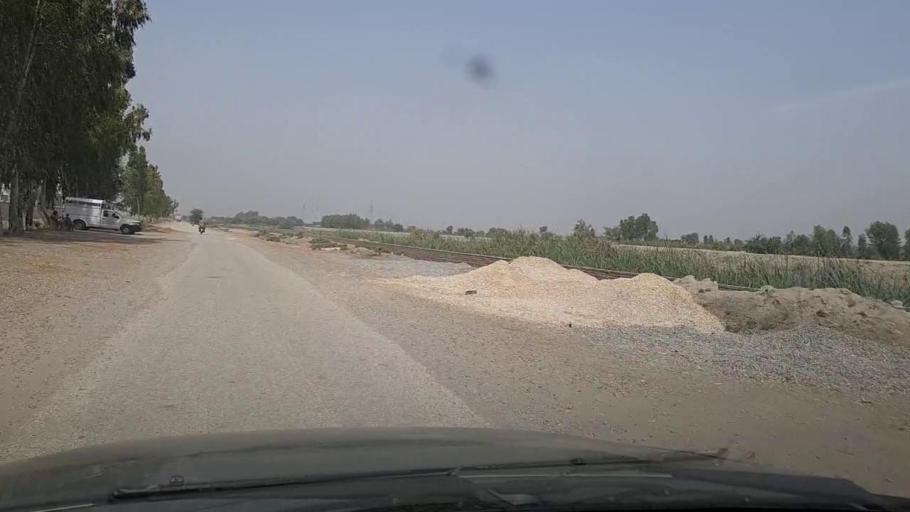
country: PK
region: Sindh
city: Thul
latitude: 28.3223
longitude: 68.7505
